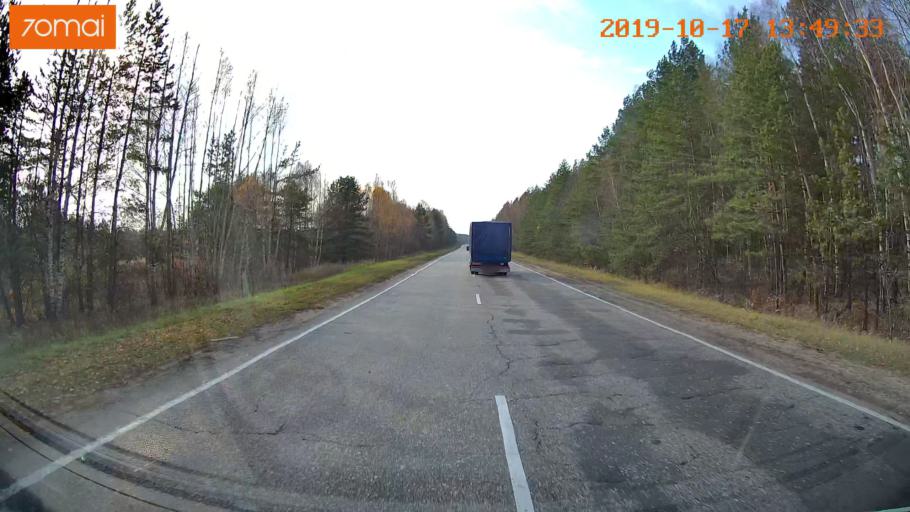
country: RU
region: Rjazan
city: Tuma
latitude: 55.1447
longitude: 40.4304
